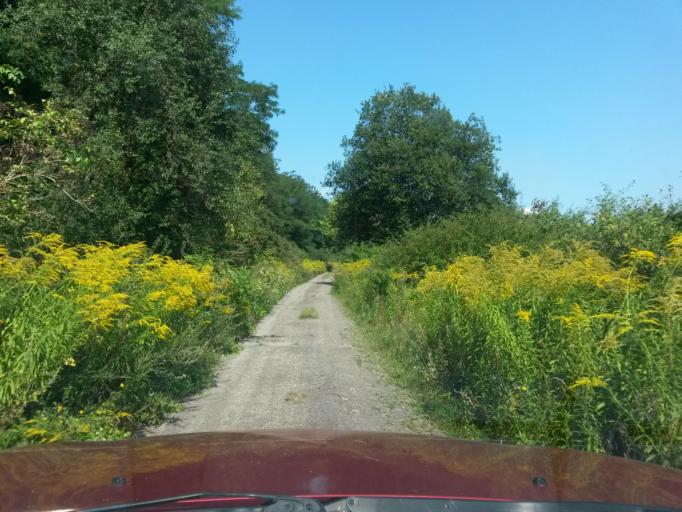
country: HU
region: Borsod-Abauj-Zemplen
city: Gonc
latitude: 48.5253
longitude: 21.1942
